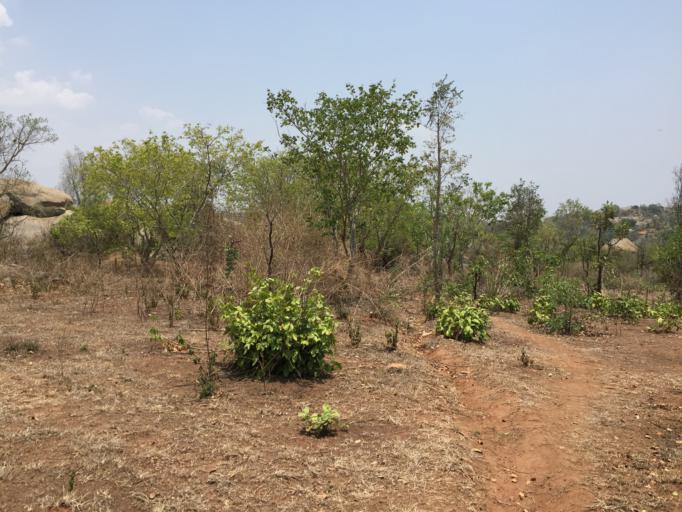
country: IN
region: Karnataka
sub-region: Bangalore Urban
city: Bangalore
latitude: 12.8870
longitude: 77.5281
